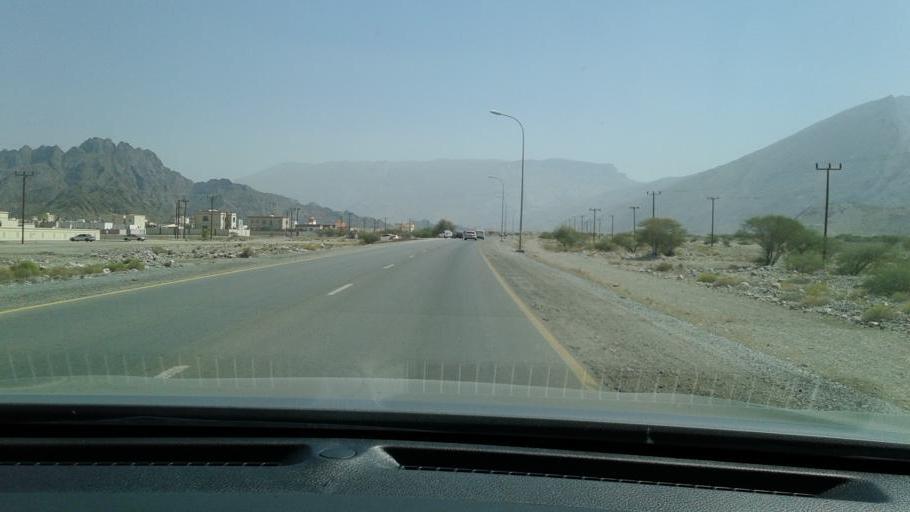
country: OM
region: Al Batinah
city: Rustaq
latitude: 23.3593
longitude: 57.4805
